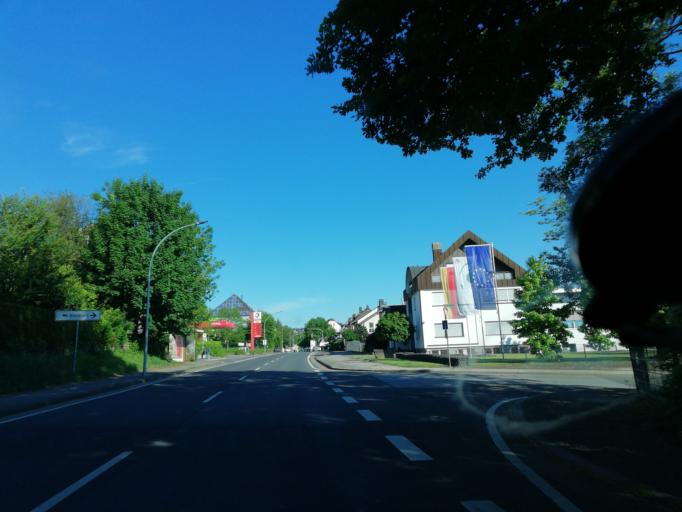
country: DE
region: North Rhine-Westphalia
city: Wetter (Ruhr)
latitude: 51.3962
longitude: 7.3531
